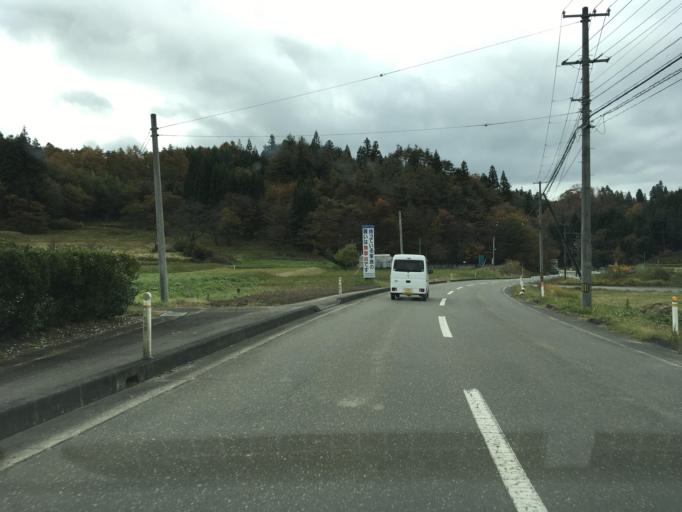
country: JP
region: Iwate
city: Mizusawa
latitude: 39.0605
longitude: 141.3619
